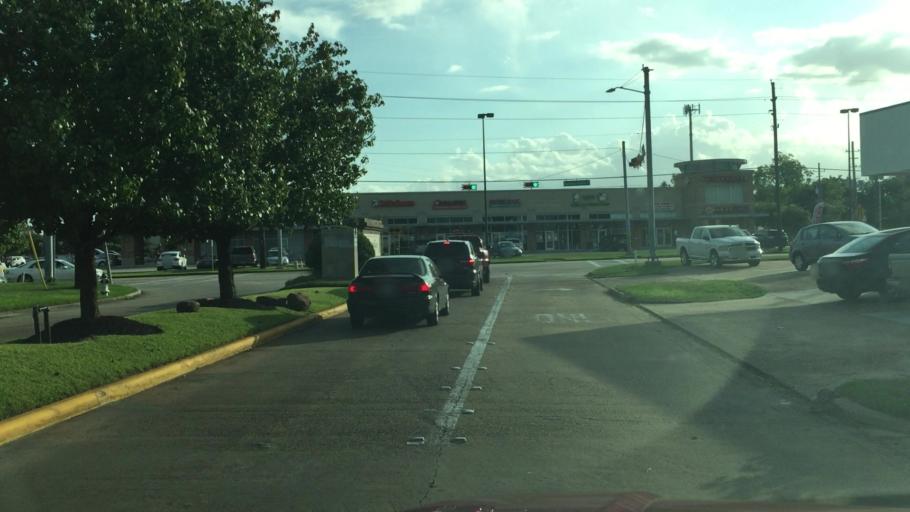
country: US
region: Texas
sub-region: Harris County
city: Tomball
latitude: 30.0235
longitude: -95.5257
